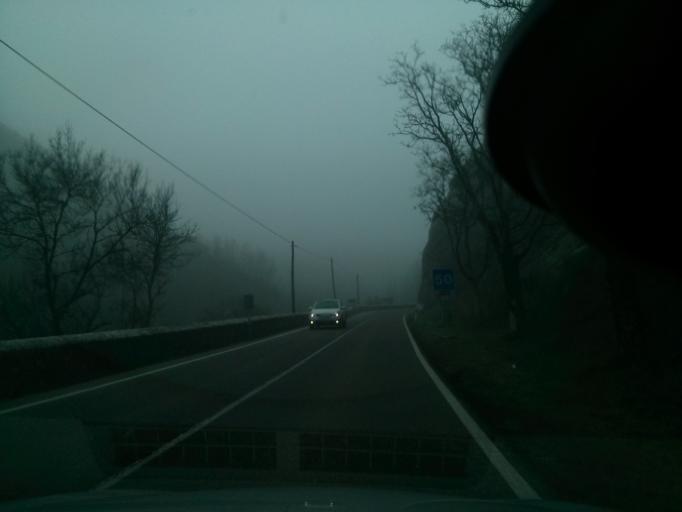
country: ES
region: Castille and Leon
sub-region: Provincia de Burgos
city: Rucandio
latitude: 42.8580
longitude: -3.5926
